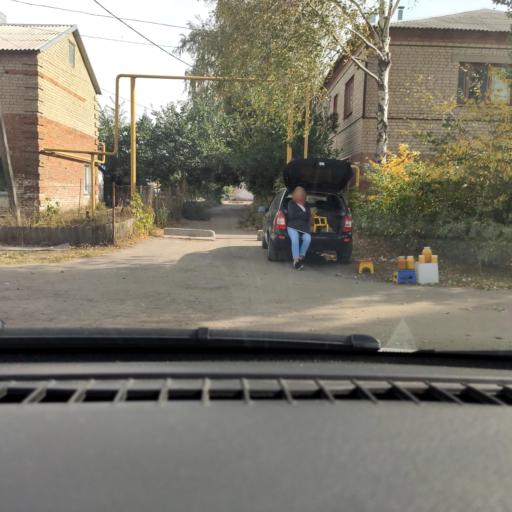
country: RU
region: Voronezj
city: Novaya Usman'
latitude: 51.6122
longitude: 39.3747
